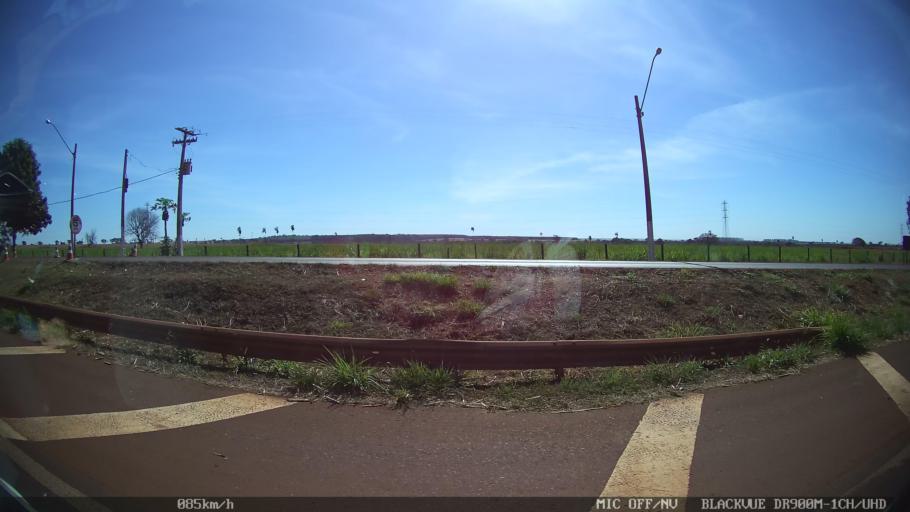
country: BR
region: Sao Paulo
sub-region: Barretos
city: Barretos
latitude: -20.4847
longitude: -48.5112
